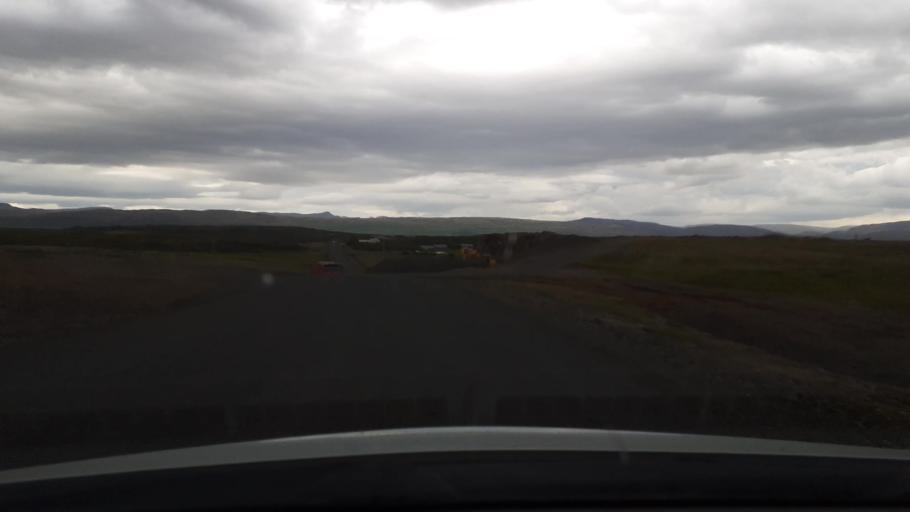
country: IS
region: West
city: Borgarnes
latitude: 64.6683
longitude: -21.6983
